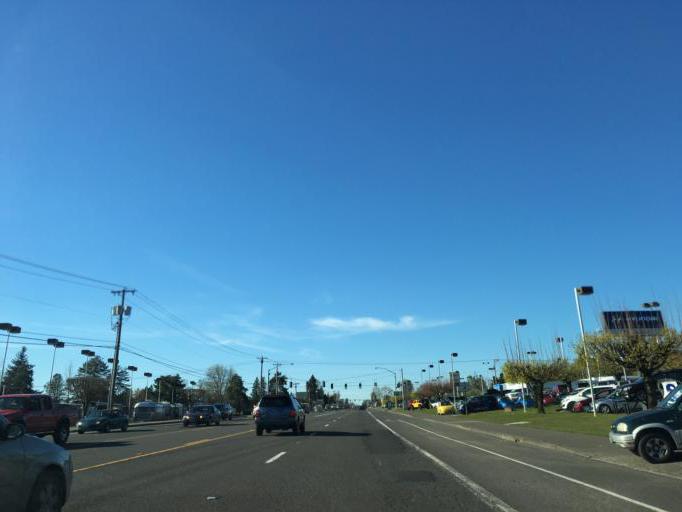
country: US
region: Oregon
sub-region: Clackamas County
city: Jennings Lodge
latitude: 45.4004
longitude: -122.6199
